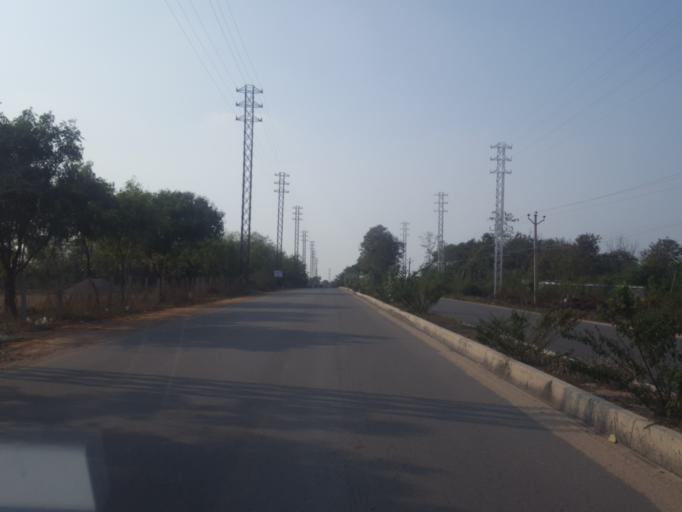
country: IN
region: Telangana
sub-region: Medak
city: Serilingampalle
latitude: 17.4146
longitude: 78.2622
